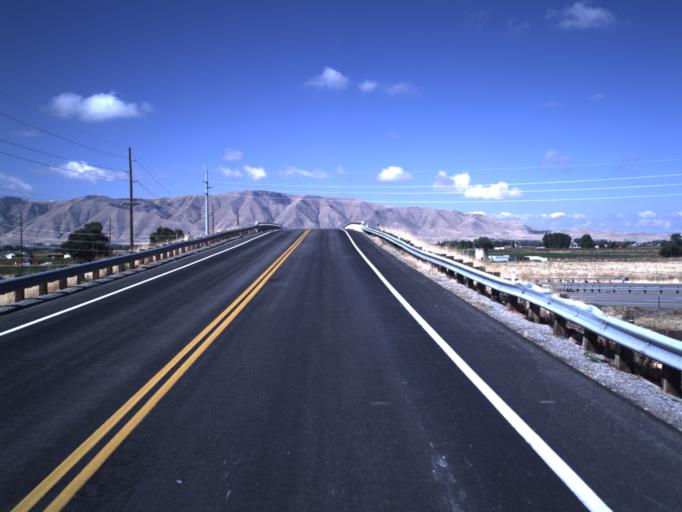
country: US
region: Utah
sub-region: Utah County
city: Spanish Fork
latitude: 40.0984
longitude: -111.6883
